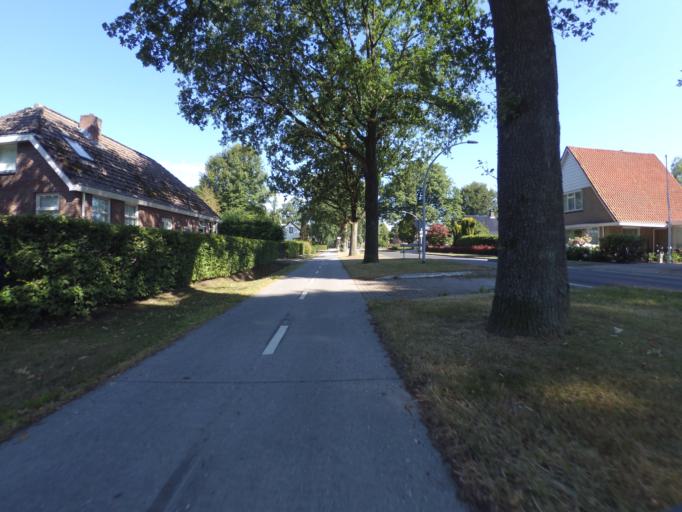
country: NL
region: Drenthe
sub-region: Gemeente Borger-Odoorn
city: Borger
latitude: 52.8619
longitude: 6.7466
